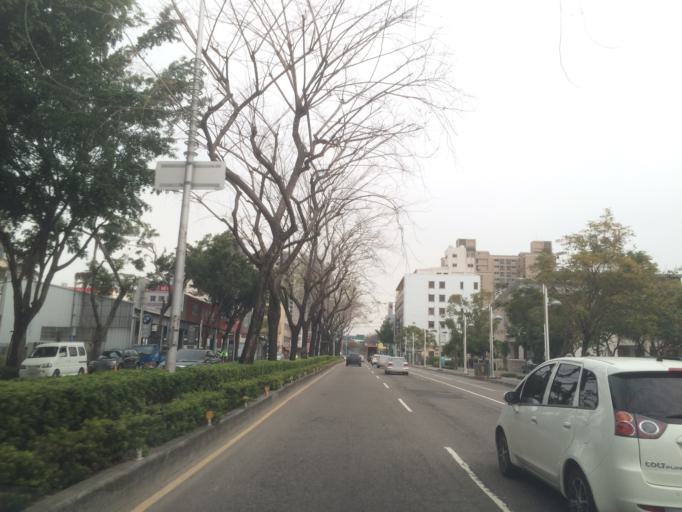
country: TW
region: Taiwan
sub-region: Taichung City
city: Taichung
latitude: 24.1918
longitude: 120.6864
